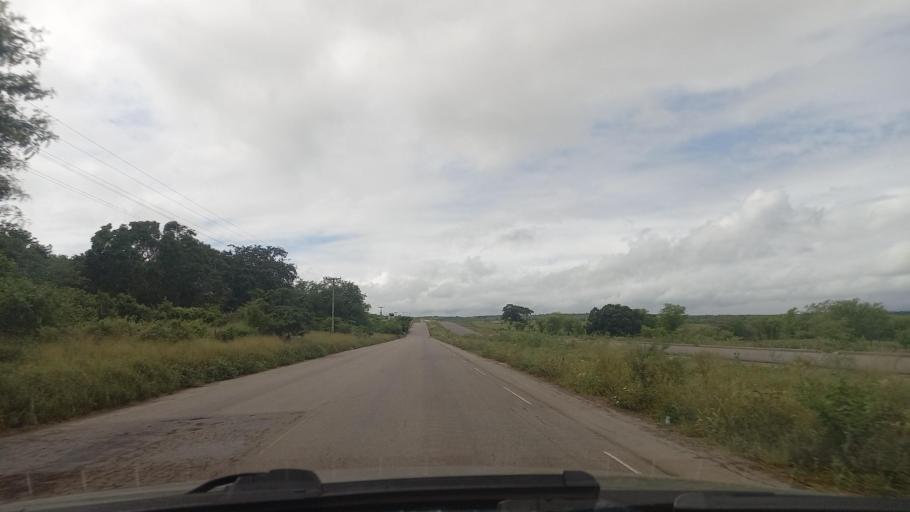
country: BR
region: Alagoas
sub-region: Batalha
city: Batalha
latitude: -9.6511
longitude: -37.1829
